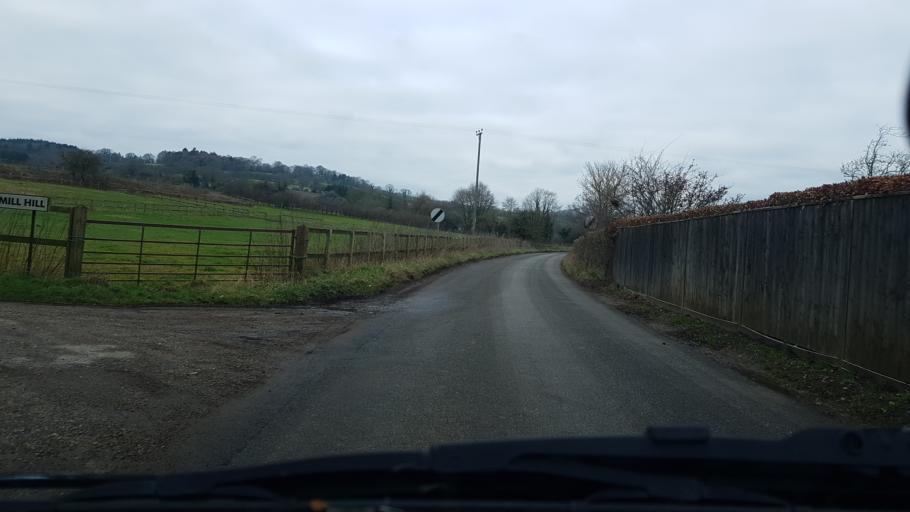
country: GB
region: England
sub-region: Hampshire
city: Andover
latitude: 51.2817
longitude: -1.4625
